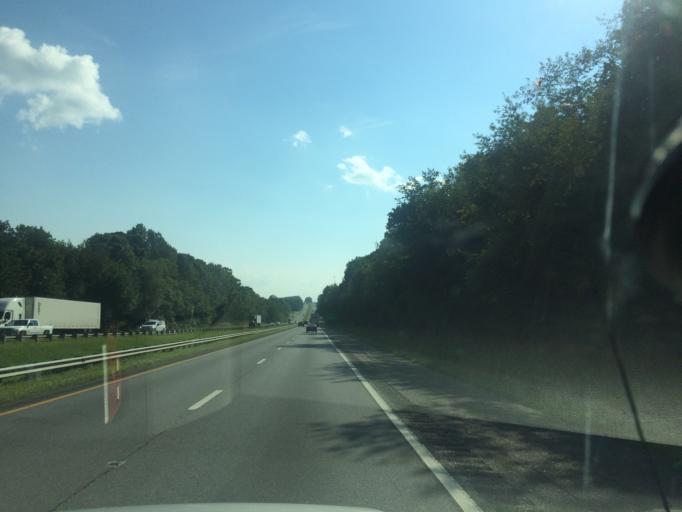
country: US
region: North Carolina
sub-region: Cleveland County
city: White Plains
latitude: 35.1930
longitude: -81.3964
